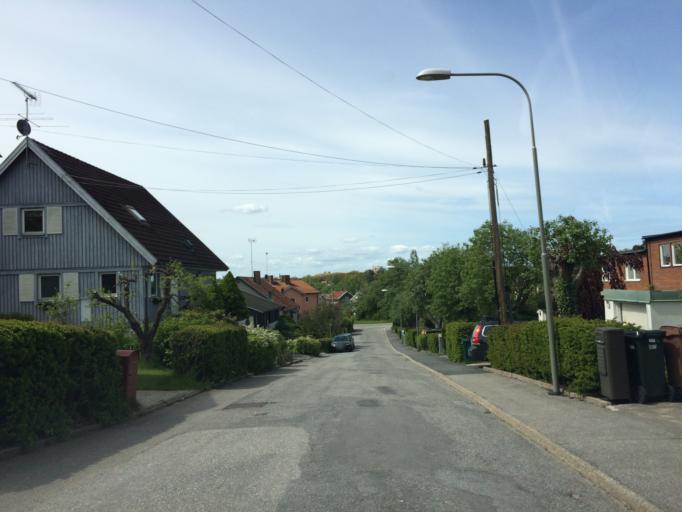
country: SE
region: Stockholm
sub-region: Huddinge Kommun
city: Huddinge
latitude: 59.2860
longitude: 17.9966
